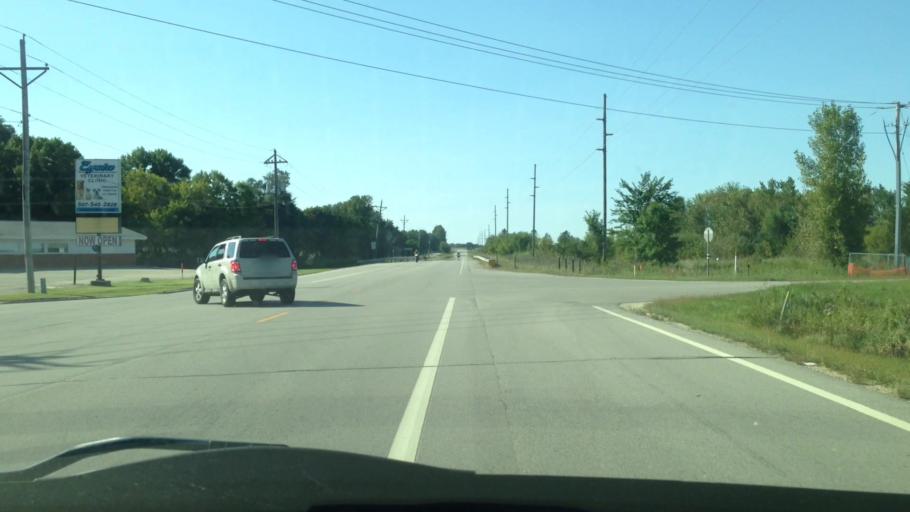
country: US
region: Minnesota
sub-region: Olmsted County
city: Eyota
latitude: 43.9911
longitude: -92.2287
